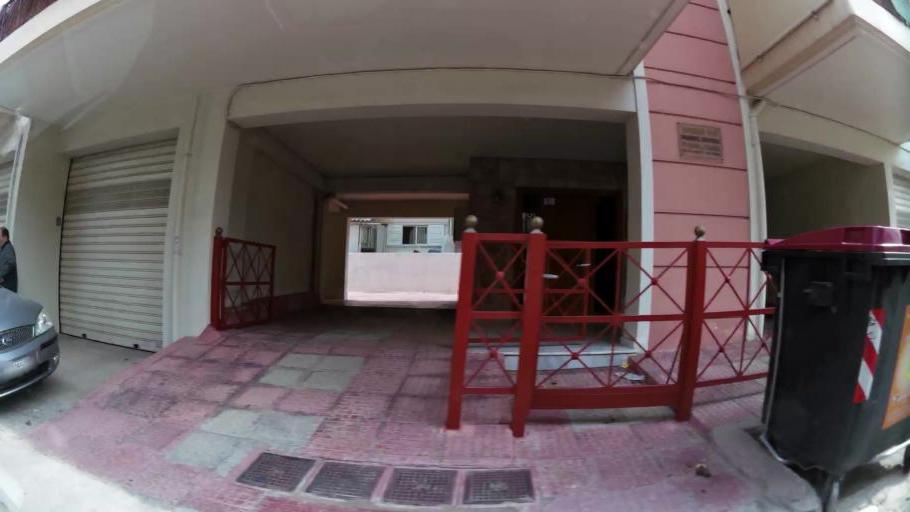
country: GR
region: Attica
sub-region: Nomarchia Athinas
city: Peristeri
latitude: 38.0110
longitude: 23.6848
